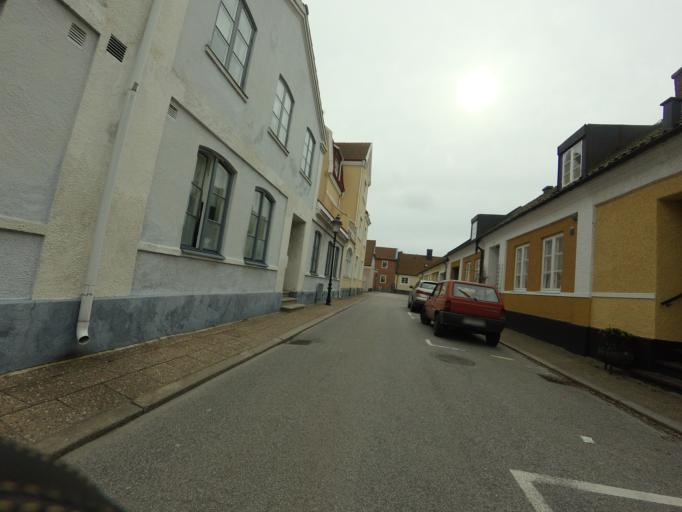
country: SE
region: Skane
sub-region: Ystads Kommun
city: Ystad
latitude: 55.4314
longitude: 13.8218
